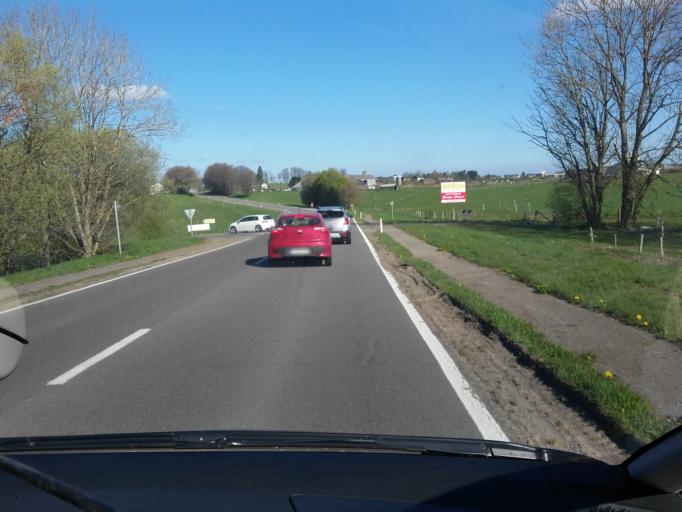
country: BE
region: Wallonia
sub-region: Province du Luxembourg
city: Neufchateau
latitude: 49.9032
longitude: 5.3739
